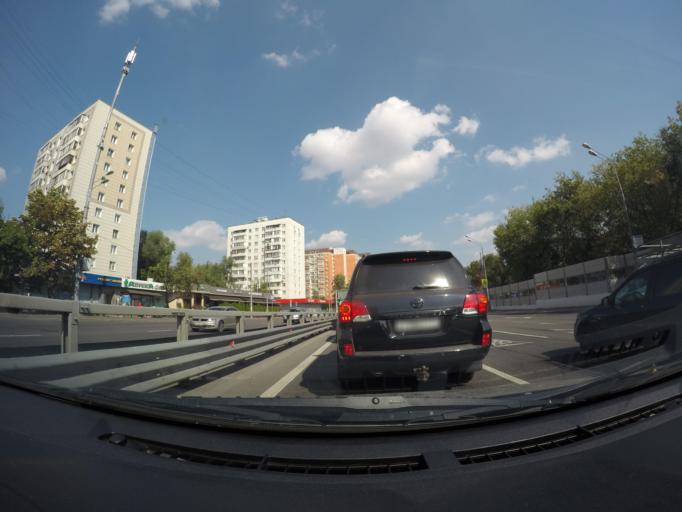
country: RU
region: Moscow
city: Zapadnoye Degunino
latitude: 55.8728
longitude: 37.5206
